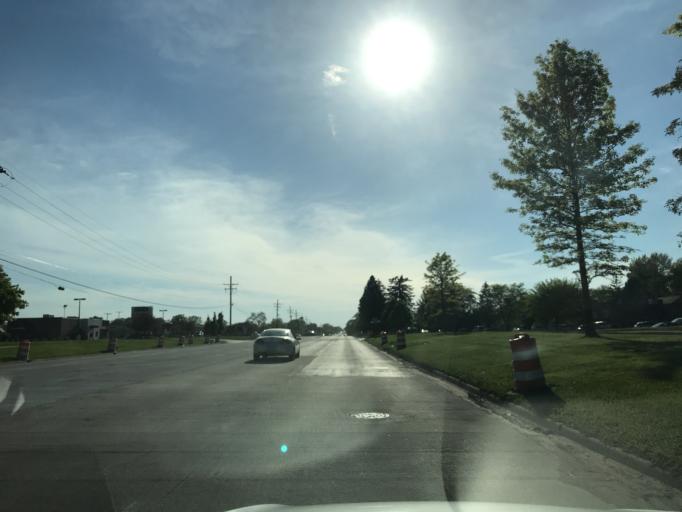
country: US
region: Michigan
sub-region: Oakland County
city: Farmington
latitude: 42.4406
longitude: -83.3781
